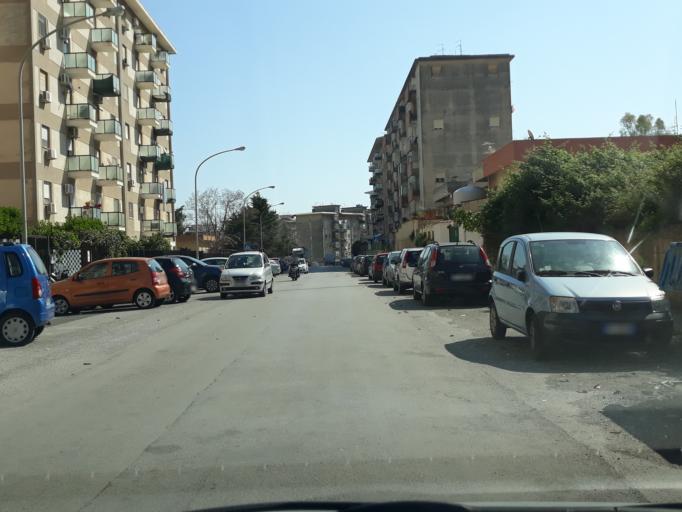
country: IT
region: Sicily
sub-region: Palermo
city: Piano dei Geli
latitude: 38.1247
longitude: 13.2934
